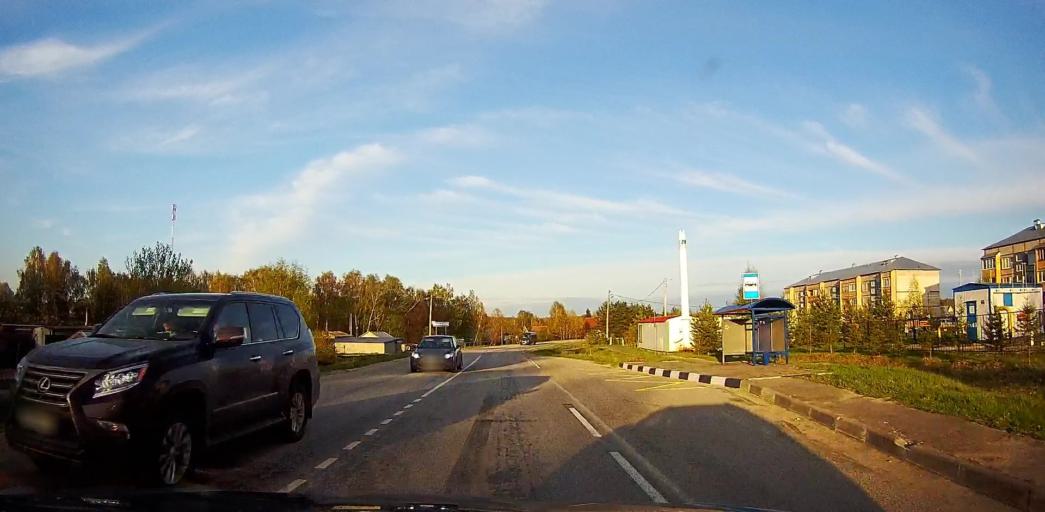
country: RU
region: Moskovskaya
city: Meshcherino
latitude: 55.2338
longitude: 38.3603
